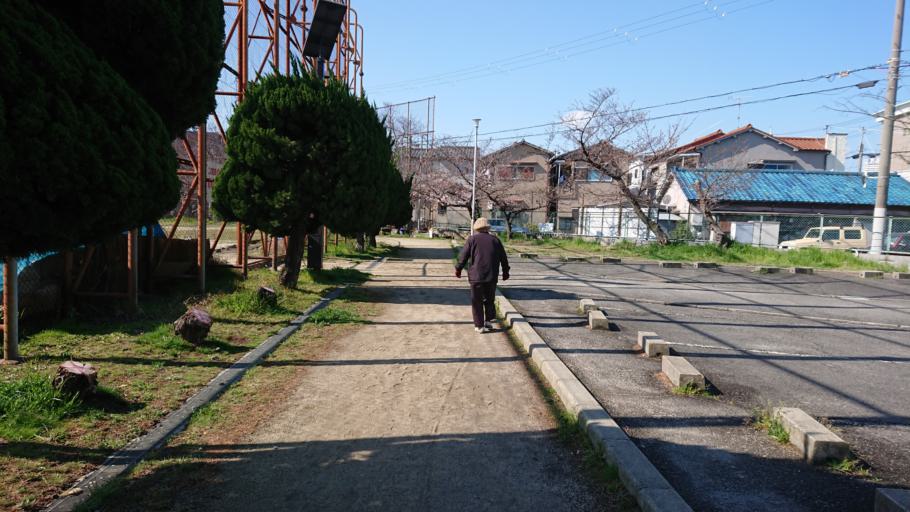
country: JP
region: Osaka
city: Takaishi
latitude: 34.5051
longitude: 135.4190
